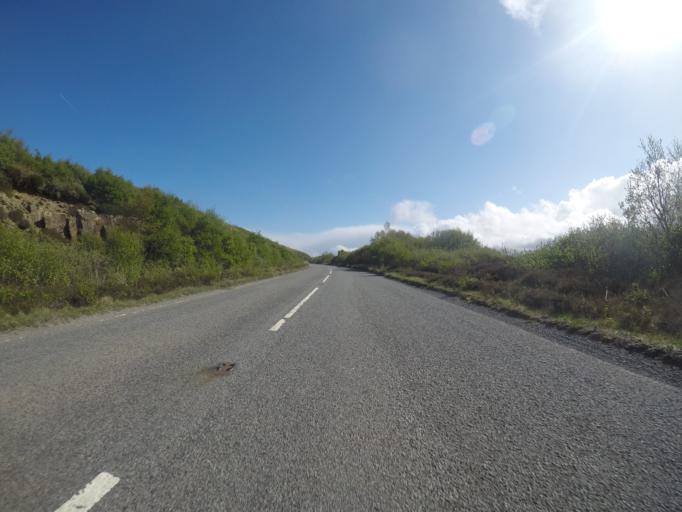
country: GB
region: Scotland
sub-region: Highland
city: Portree
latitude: 57.6083
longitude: -6.1740
